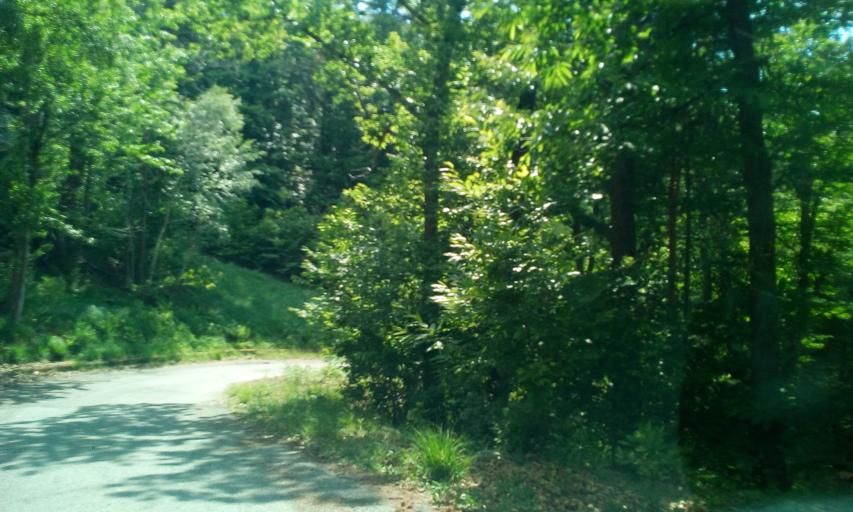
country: IT
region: Aosta Valley
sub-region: Valle d'Aosta
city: Chatillon
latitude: 45.7320
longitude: 7.6308
